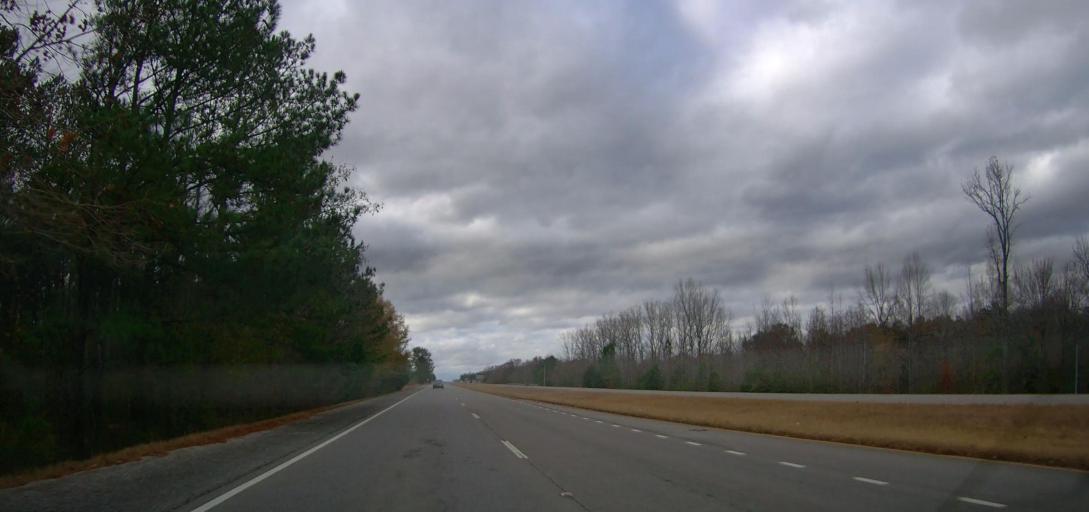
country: US
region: Alabama
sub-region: Lawrence County
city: Town Creek
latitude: 34.5833
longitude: -87.4148
